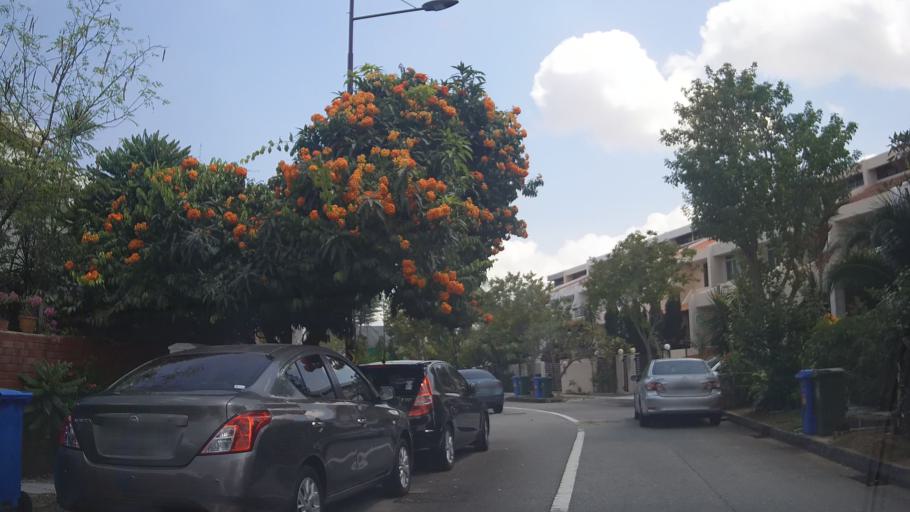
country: SG
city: Singapore
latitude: 1.3247
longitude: 103.9543
